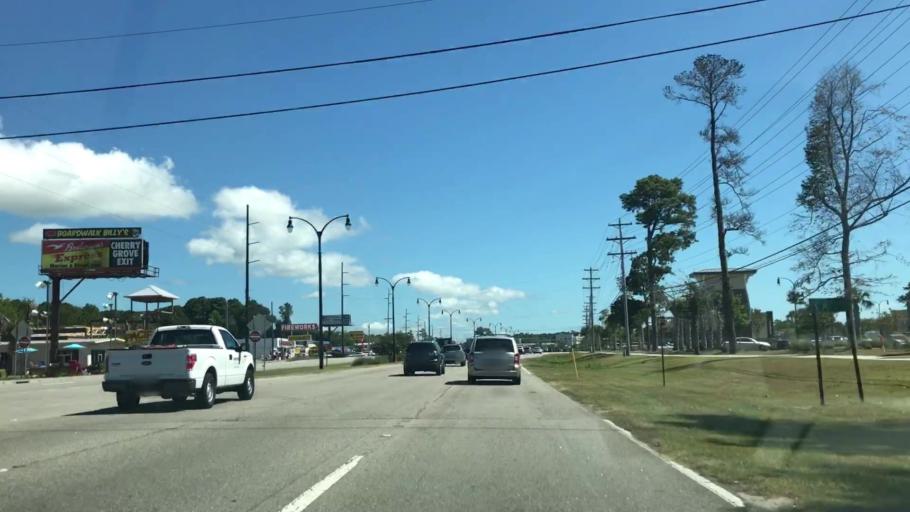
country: US
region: South Carolina
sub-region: Horry County
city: North Myrtle Beach
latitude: 33.8395
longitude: -78.6657
